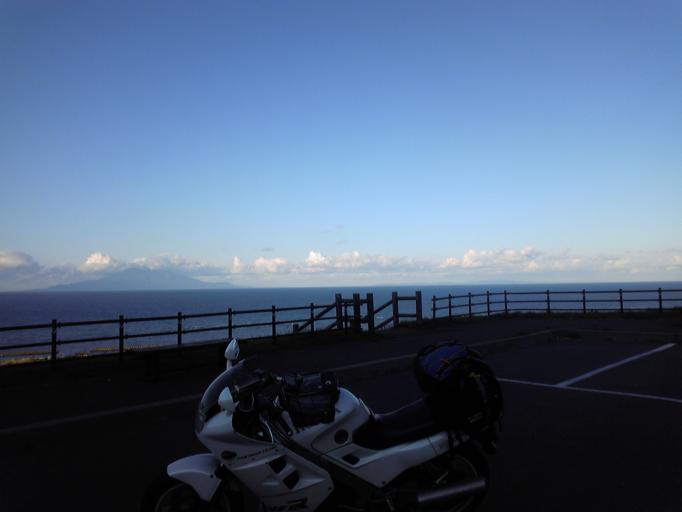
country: JP
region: Hokkaido
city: Wakkanai
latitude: 45.3802
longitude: 141.6537
